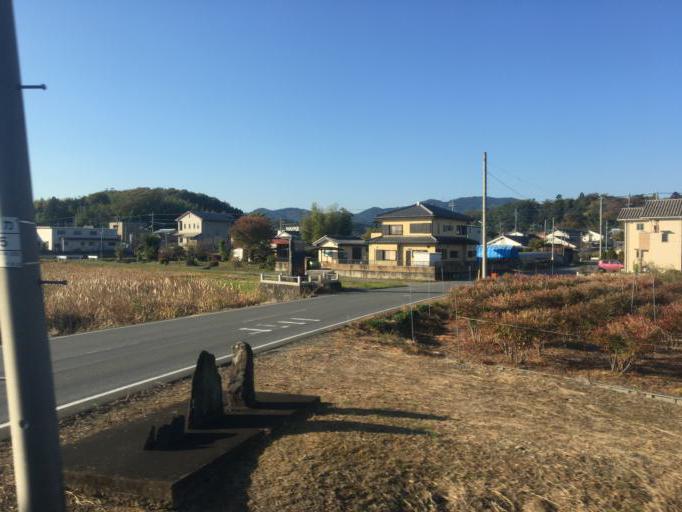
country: JP
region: Saitama
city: Kodamacho-kodamaminami
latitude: 36.1710
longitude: 139.1843
